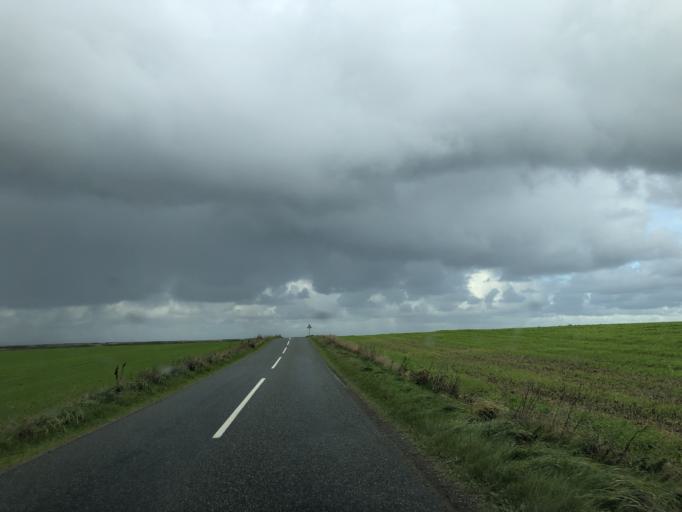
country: DK
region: Central Jutland
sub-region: Lemvig Kommune
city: Harboore
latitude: 56.5474
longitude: 8.1445
